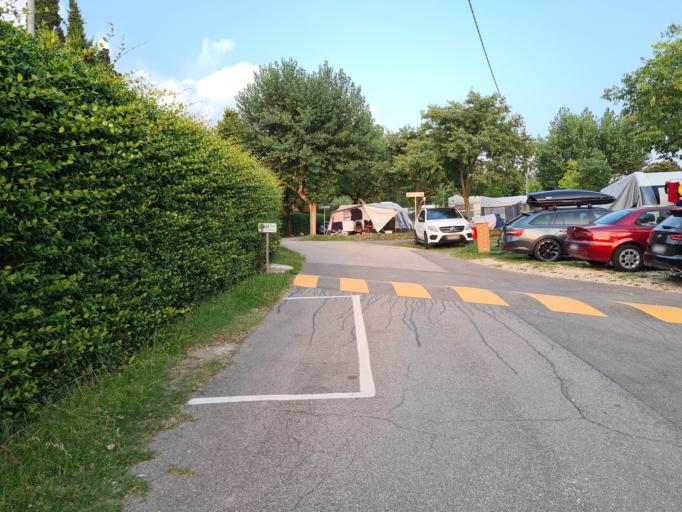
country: IT
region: Veneto
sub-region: Provincia di Verona
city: Lazise
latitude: 45.4930
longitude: 10.7329
